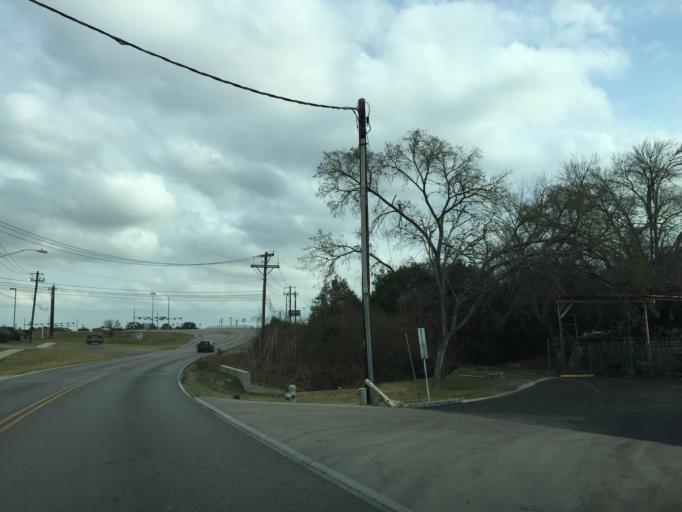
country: US
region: Texas
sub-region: Travis County
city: Wells Branch
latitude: 30.4008
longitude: -97.6767
